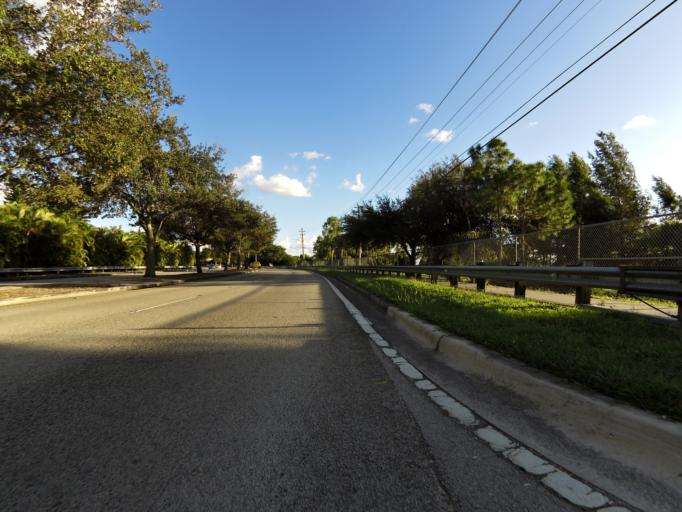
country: US
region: Florida
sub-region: Broward County
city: Cooper City
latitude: 26.0723
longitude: -80.2649
